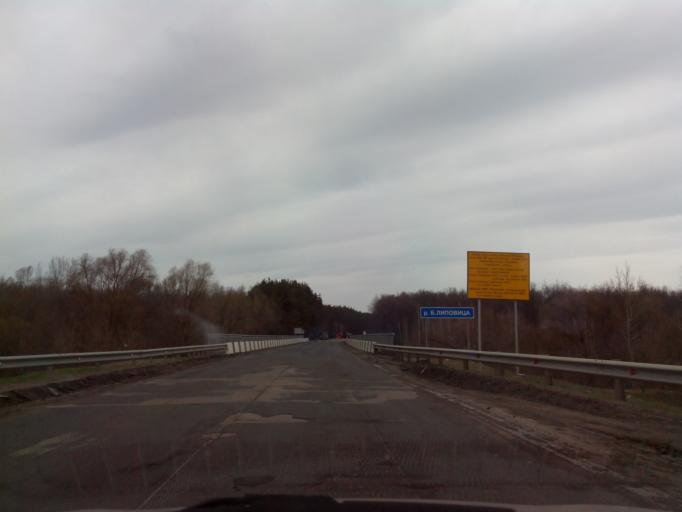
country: RU
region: Tambov
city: Znamenka
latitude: 52.5311
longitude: 41.3571
